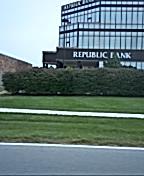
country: US
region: Kentucky
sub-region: Jefferson County
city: Hurstbourne
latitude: 38.2377
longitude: -85.5769
